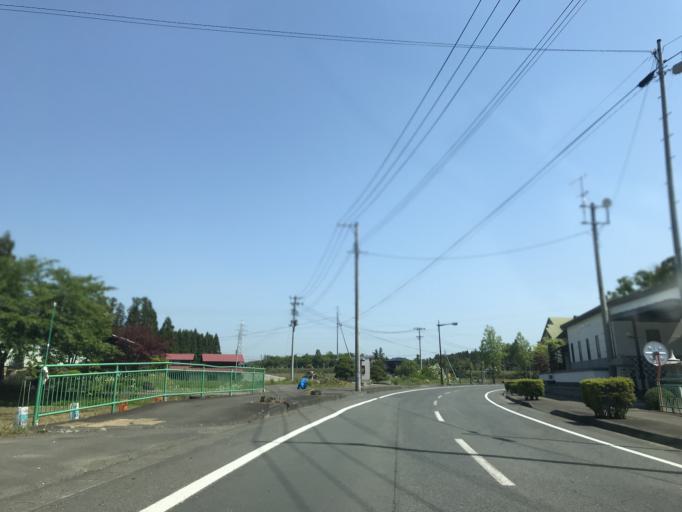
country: JP
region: Iwate
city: Kitakami
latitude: 39.2126
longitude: 141.0962
